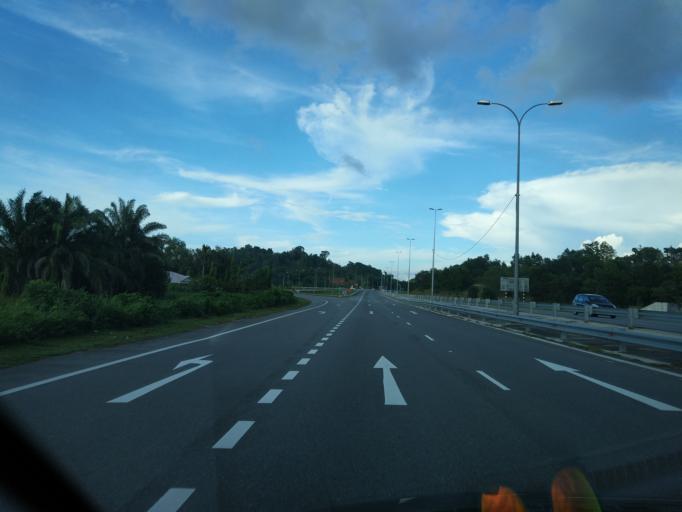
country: BN
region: Belait
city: Seria
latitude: 4.6511
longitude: 114.4668
